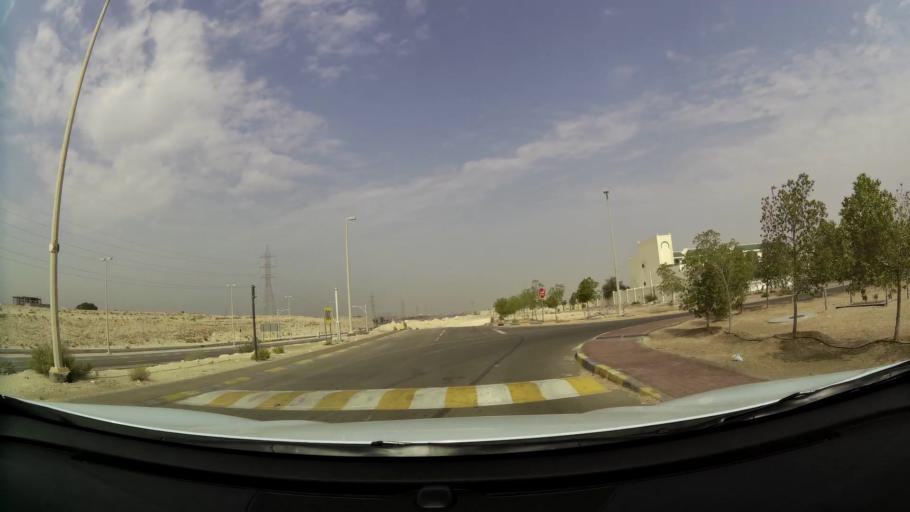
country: AE
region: Abu Dhabi
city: Abu Dhabi
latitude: 24.2979
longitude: 54.6602
